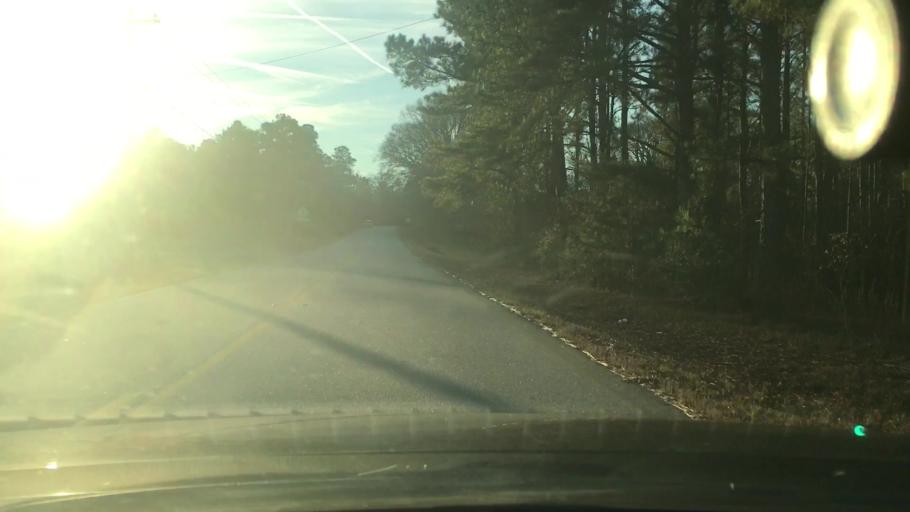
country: US
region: Georgia
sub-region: Coweta County
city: Senoia
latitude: 33.3018
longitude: -84.4634
